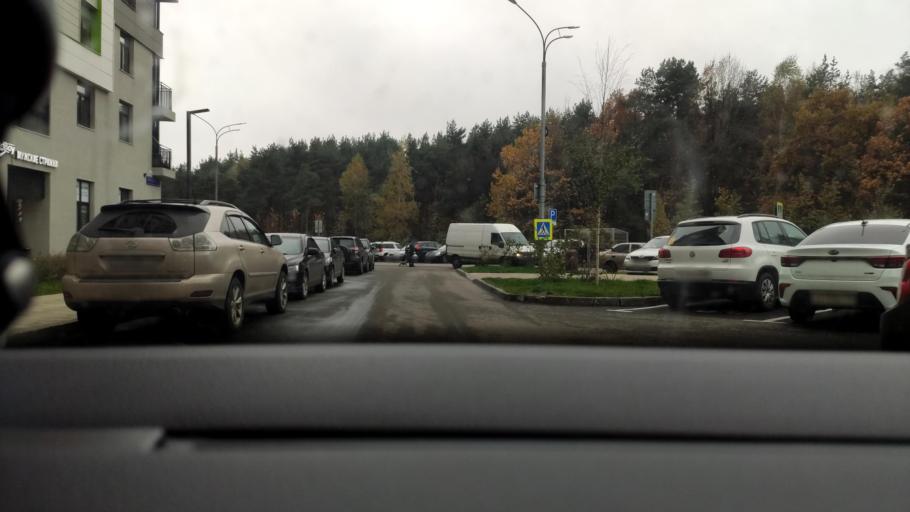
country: RU
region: Moscow
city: Zhulebino
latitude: 55.6706
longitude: 37.8549
